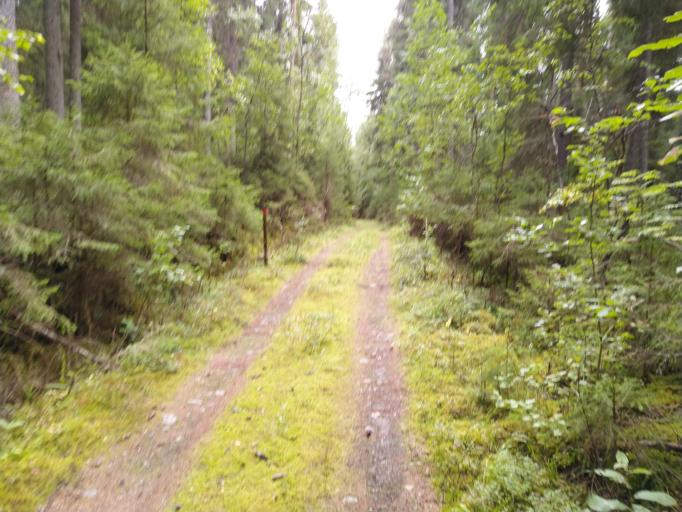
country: FI
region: Paijanne Tavastia
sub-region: Lahti
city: Auttoinen
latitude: 61.2350
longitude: 25.1695
